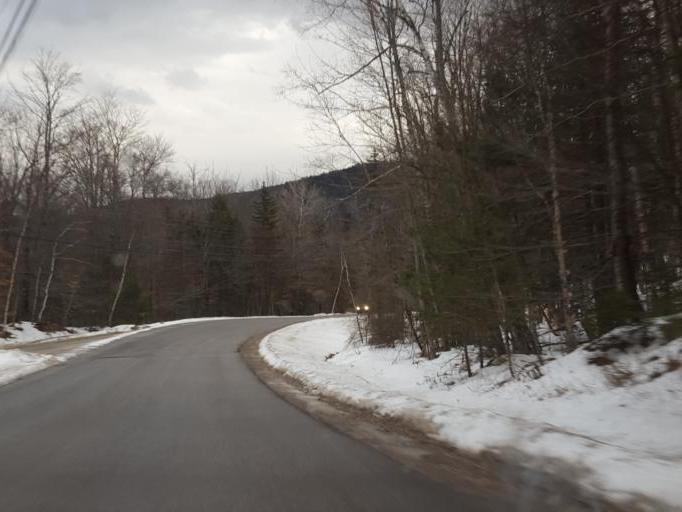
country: US
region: Vermont
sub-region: Rutland County
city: Rutland
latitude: 43.6122
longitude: -72.7625
